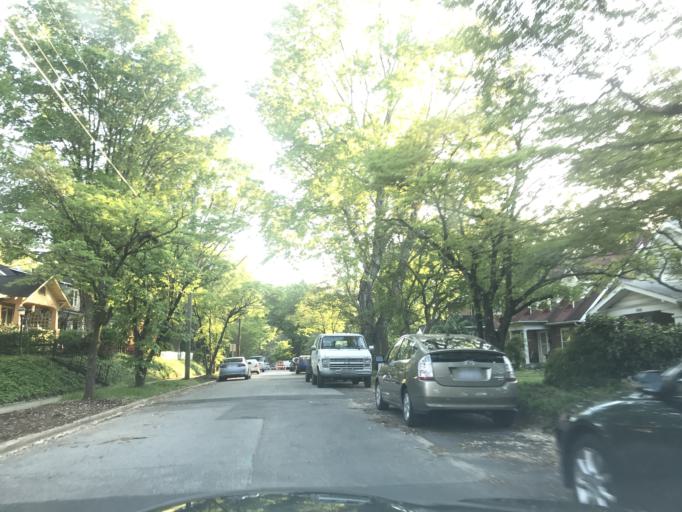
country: US
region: North Carolina
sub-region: Wake County
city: Raleigh
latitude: 35.7991
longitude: -78.6286
